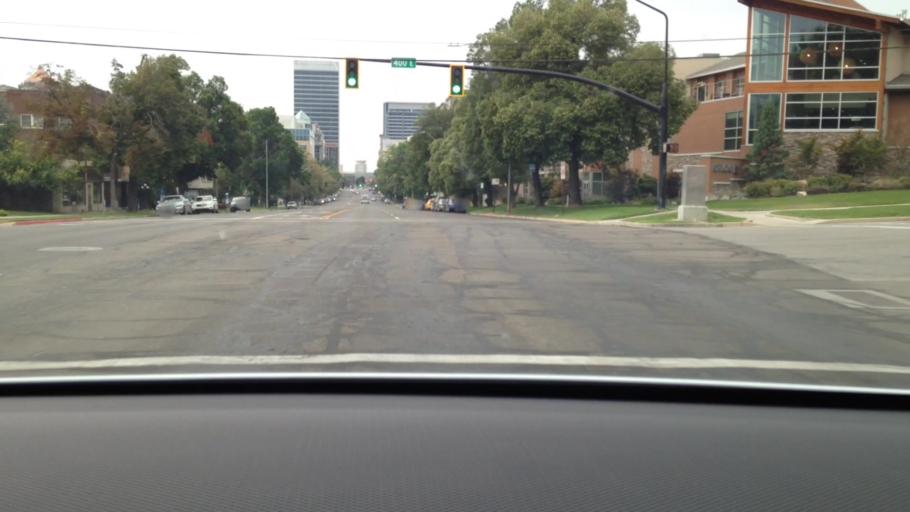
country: US
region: Utah
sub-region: Salt Lake County
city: Salt Lake City
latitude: 40.7672
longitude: -111.8793
